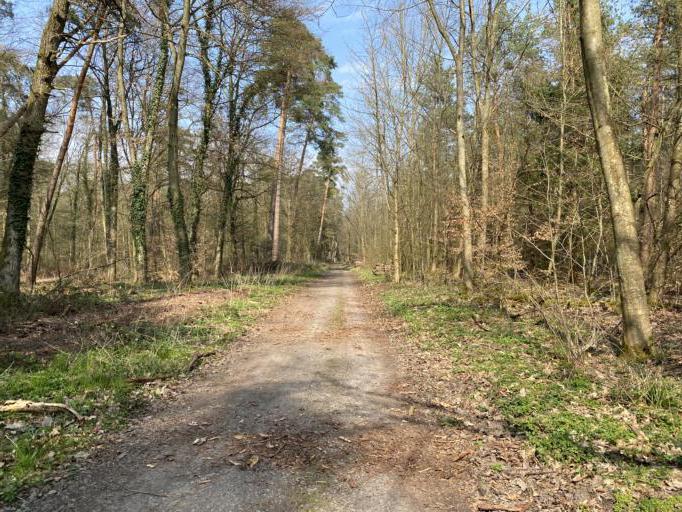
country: DE
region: Baden-Wuerttemberg
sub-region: Karlsruhe Region
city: Karlsruhe
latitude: 49.0488
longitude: 8.4120
